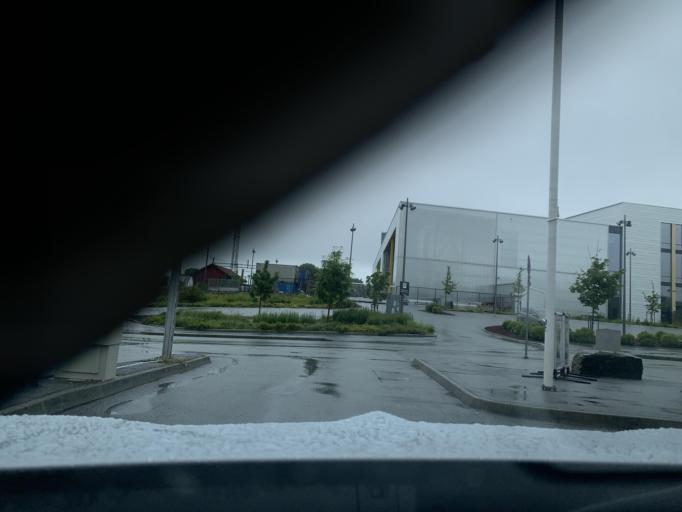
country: NO
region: Rogaland
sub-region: Time
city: Bryne
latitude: 58.7305
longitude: 5.6492
